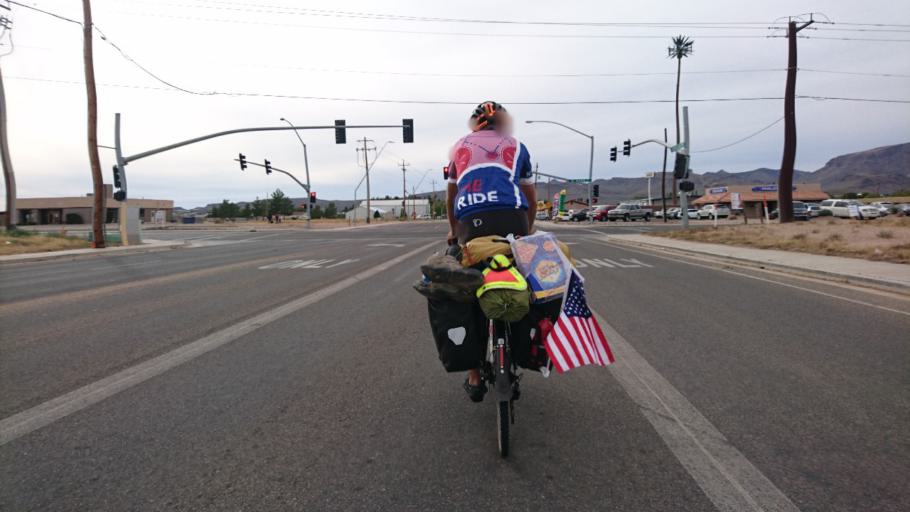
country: US
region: Arizona
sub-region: Mohave County
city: New Kingman-Butler
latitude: 35.2394
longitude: -114.0109
